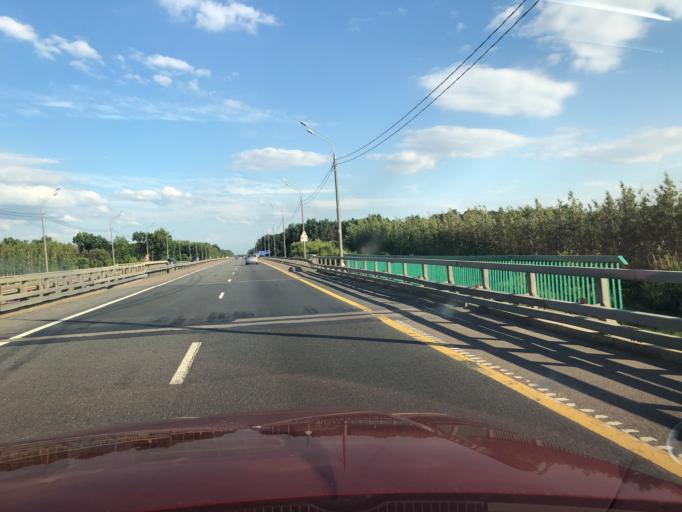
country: RU
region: Lipetsk
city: Zadonsk
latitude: 52.4244
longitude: 38.8316
